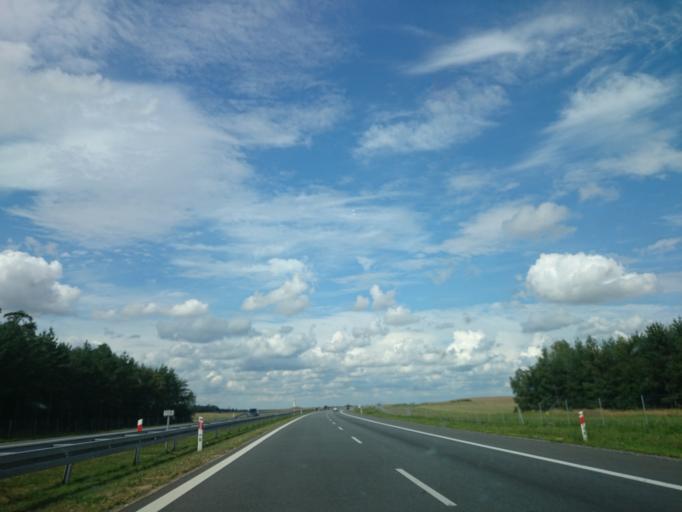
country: PL
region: Lubusz
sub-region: Powiat swiebodzinski
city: Swiebodzin
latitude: 52.2158
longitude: 15.5564
